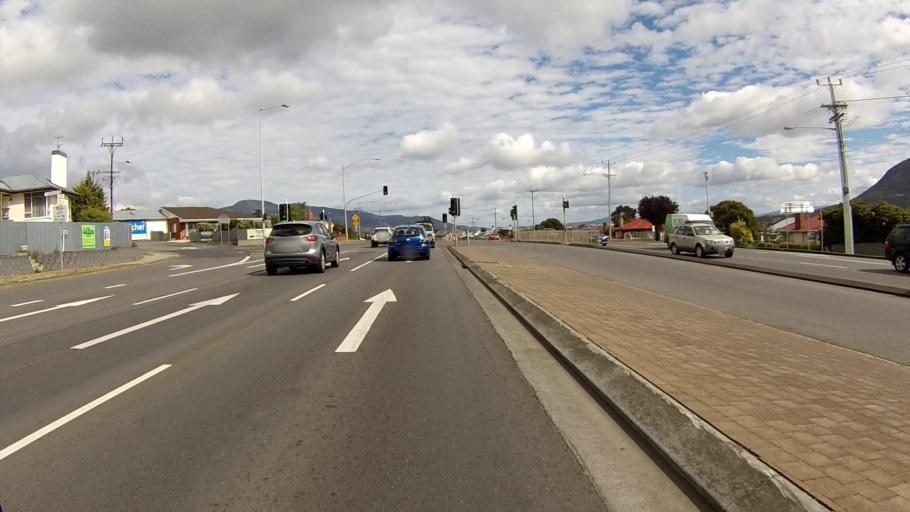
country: AU
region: Tasmania
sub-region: Glenorchy
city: Goodwood
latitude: -42.8338
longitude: 147.2983
